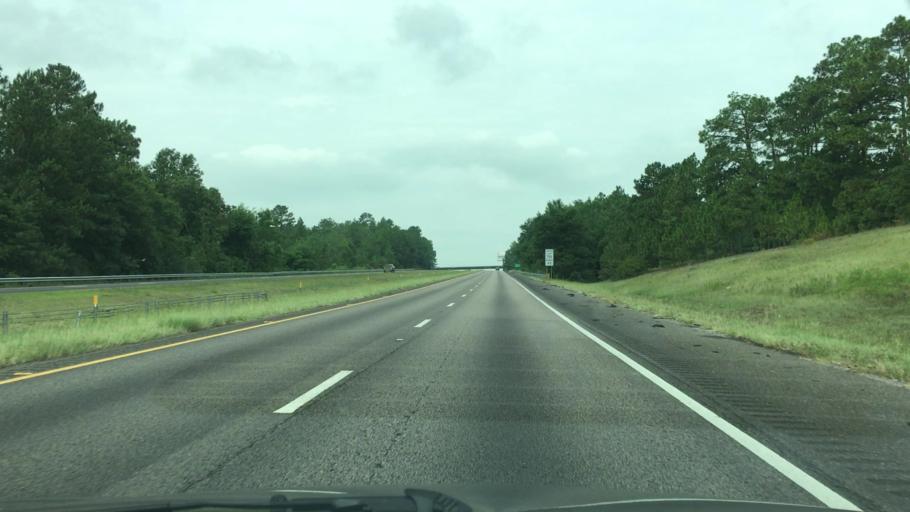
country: US
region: South Carolina
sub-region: Aiken County
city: Graniteville
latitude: 33.6032
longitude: -81.8555
